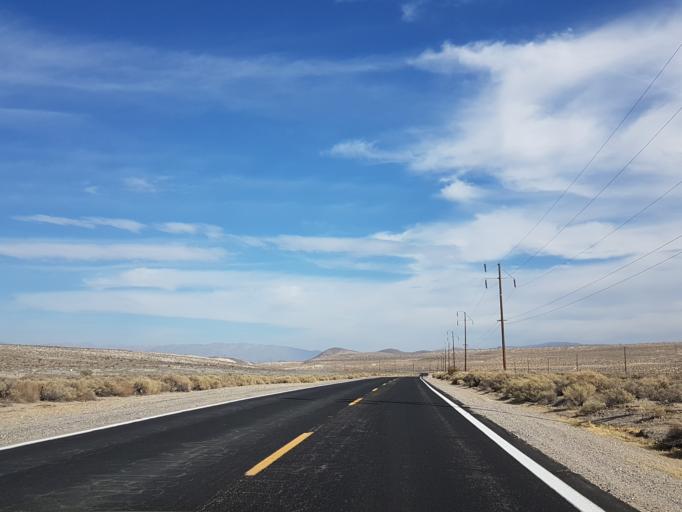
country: US
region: California
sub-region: San Bernardino County
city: Searles Valley
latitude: 35.6490
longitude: -117.4830
